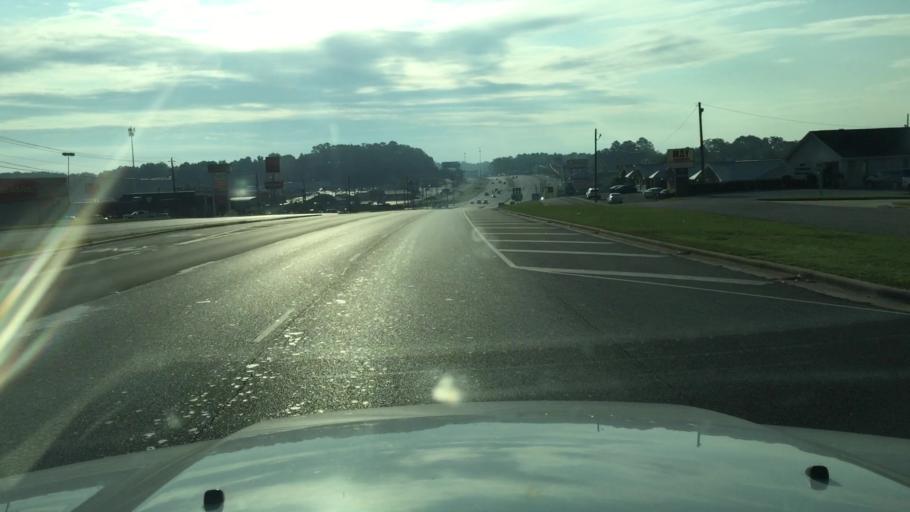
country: US
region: Alabama
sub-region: Tuscaloosa County
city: Northport
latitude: 33.2403
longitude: -87.5814
